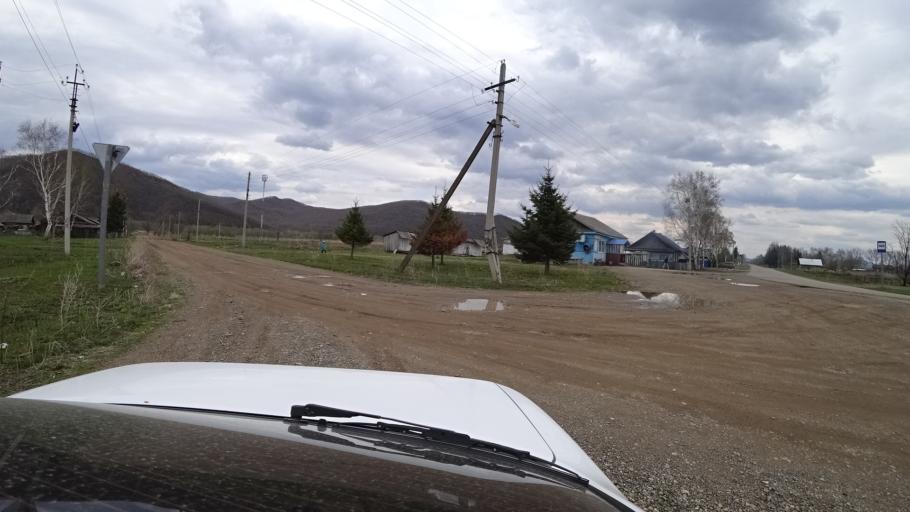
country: RU
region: Primorskiy
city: Novopokrovka
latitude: 45.5783
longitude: 134.3125
